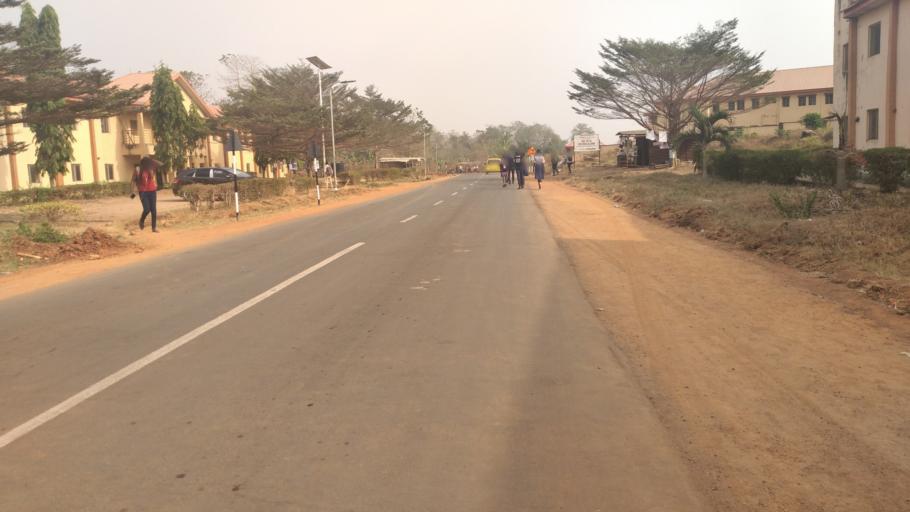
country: NG
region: Ondo
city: Ilare
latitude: 7.3022
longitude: 5.1434
